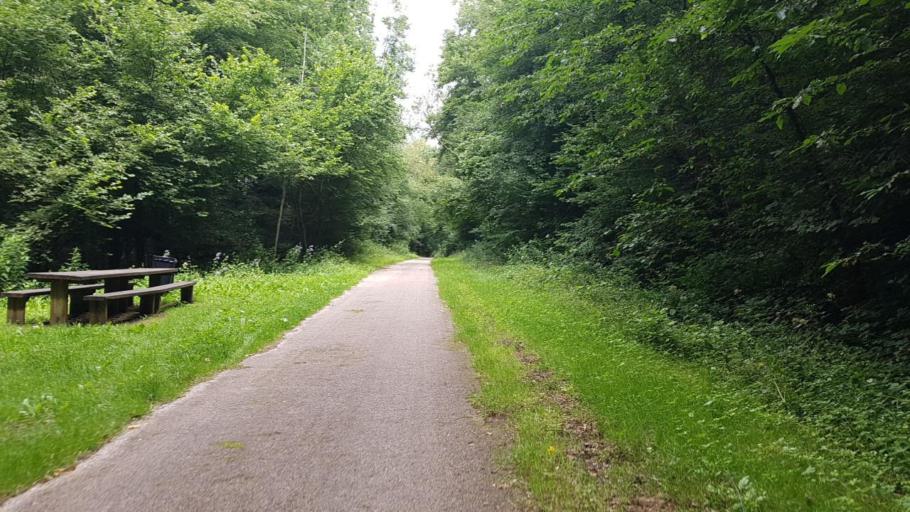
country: FR
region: Picardie
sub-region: Departement de l'Aisne
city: Esqueheries
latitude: 49.9036
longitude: 3.7600
